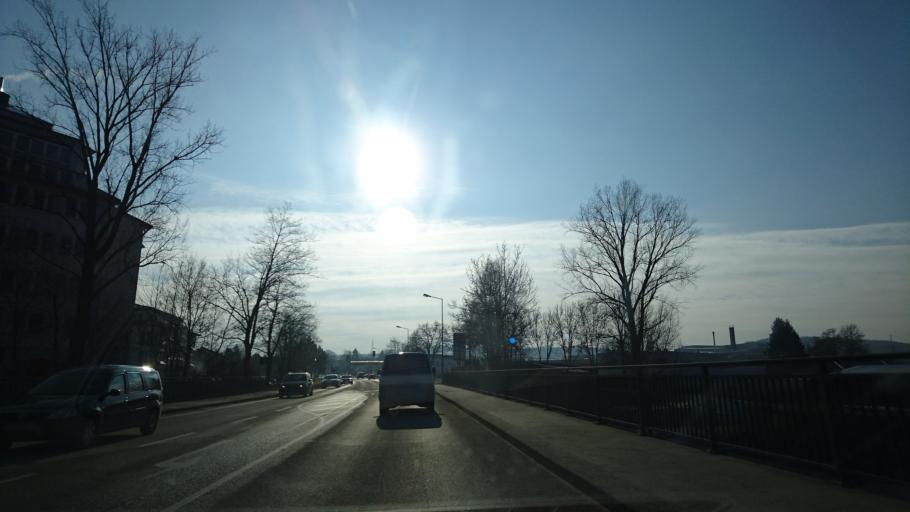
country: DE
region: Bavaria
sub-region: Lower Bavaria
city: Pfarrkirchen
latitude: 48.4239
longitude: 12.9426
